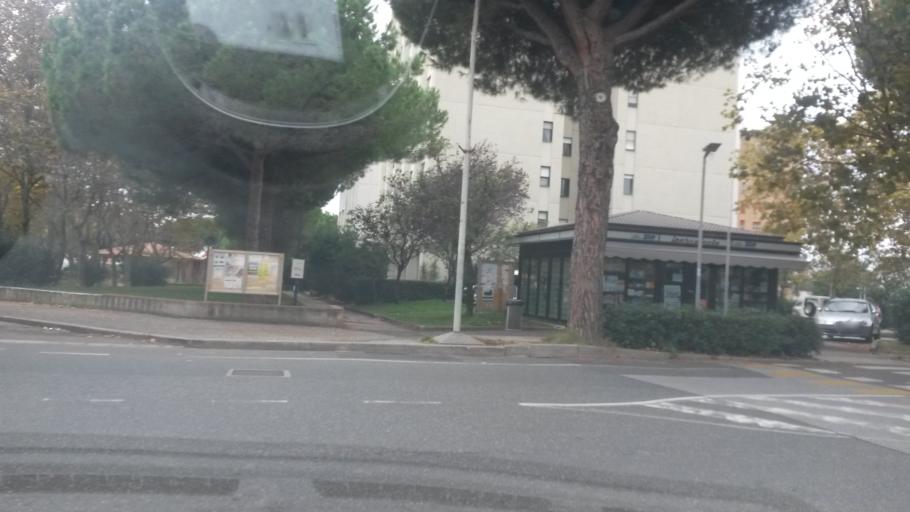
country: IT
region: Tuscany
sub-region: Provincia di Livorno
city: Rosignano Solvay-Castiglioncello
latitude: 43.3952
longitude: 10.4370
